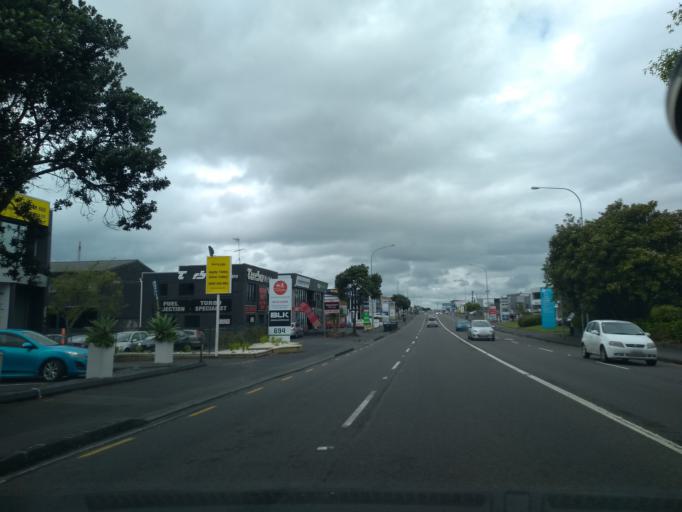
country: NZ
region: Auckland
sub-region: Auckland
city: Tamaki
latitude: -36.9042
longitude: 174.8089
